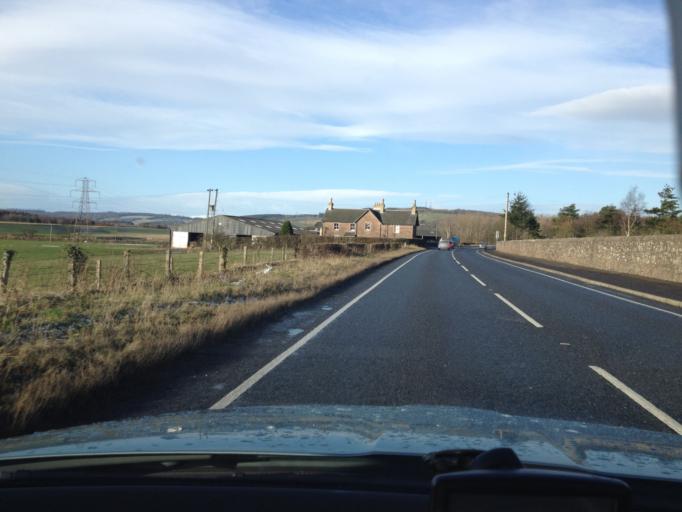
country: GB
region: Scotland
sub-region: Perth and Kinross
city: Bridge of Earn
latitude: 56.3545
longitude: -3.4081
